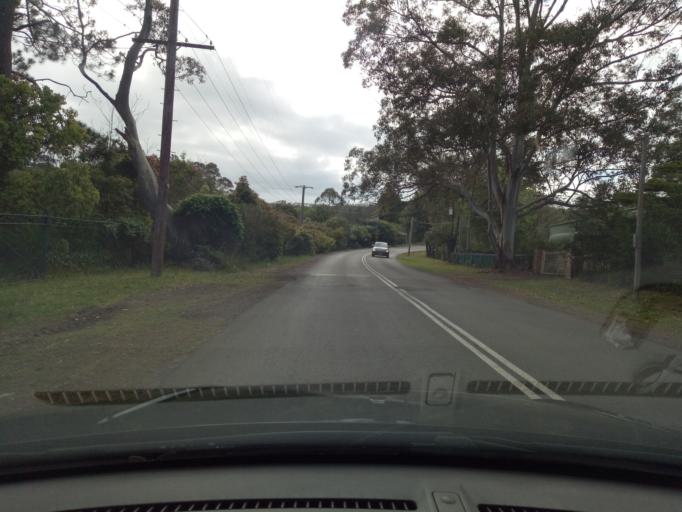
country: AU
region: New South Wales
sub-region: Gosford Shire
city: Lisarow
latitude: -33.3914
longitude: 151.3898
